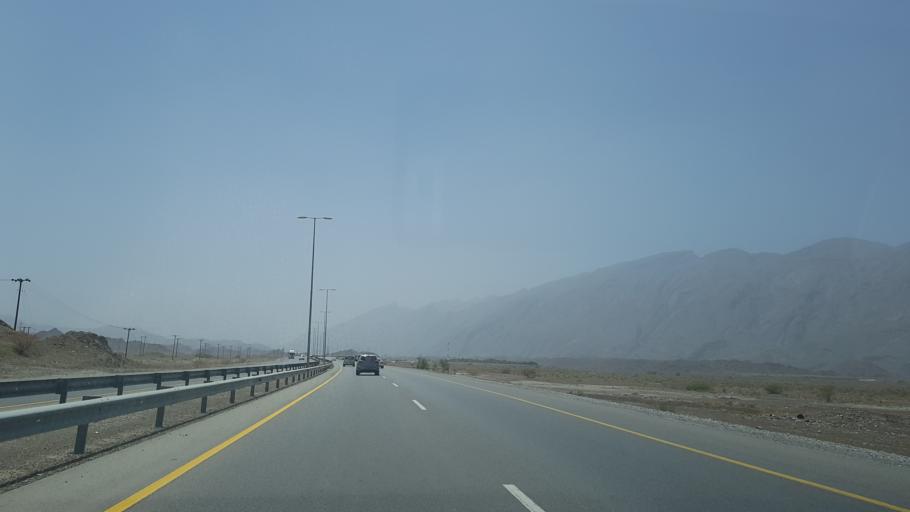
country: OM
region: Muhafazat ad Dakhiliyah
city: Sufalat Sama'il
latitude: 23.2582
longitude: 57.9309
